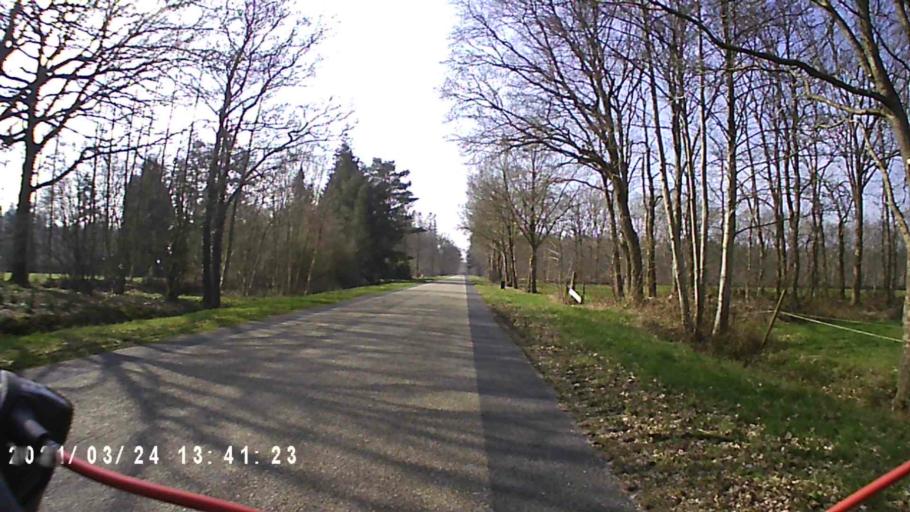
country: NL
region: Groningen
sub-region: Gemeente Leek
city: Leek
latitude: 53.0901
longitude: 6.2794
